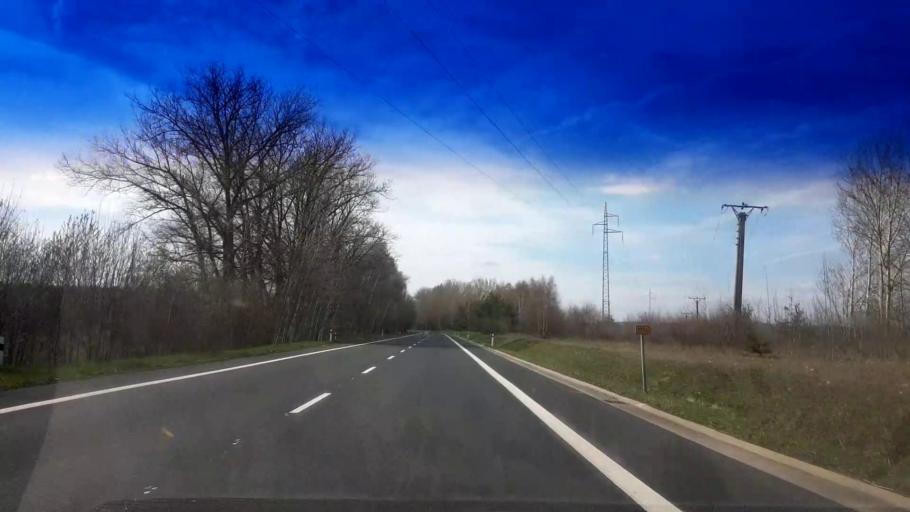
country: CZ
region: Karlovarsky
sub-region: Okres Cheb
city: Frantiskovy Lazne
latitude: 50.0969
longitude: 12.3334
